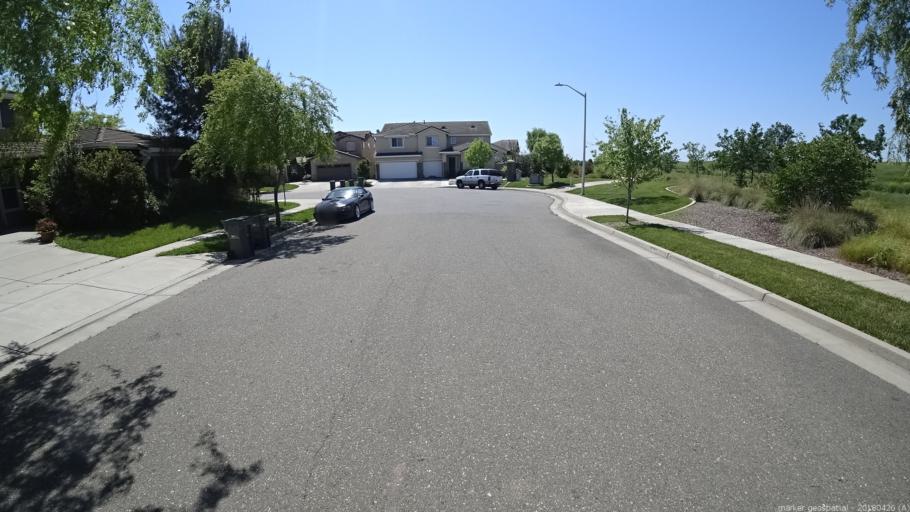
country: US
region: California
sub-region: Yolo County
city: West Sacramento
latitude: 38.5271
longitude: -121.5812
